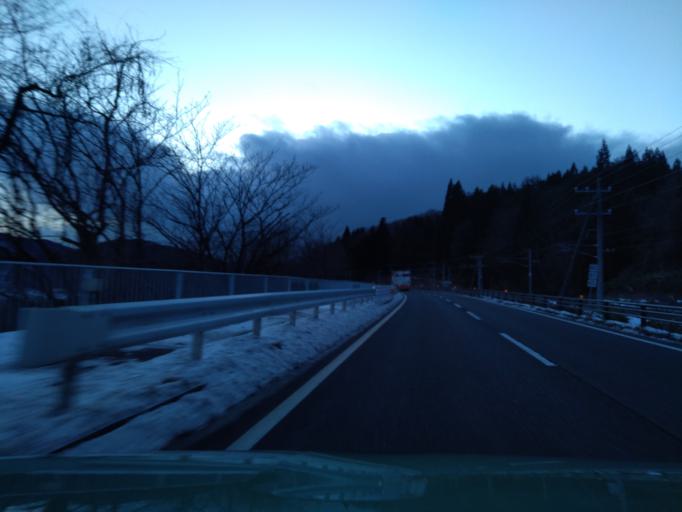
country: JP
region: Iwate
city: Shizukuishi
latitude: 39.6911
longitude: 140.9257
